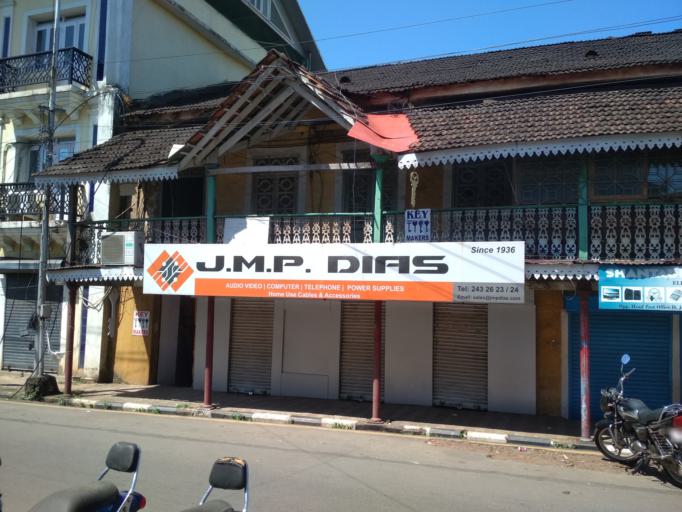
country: IN
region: Goa
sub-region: North Goa
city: Panaji
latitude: 15.4998
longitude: 73.8322
